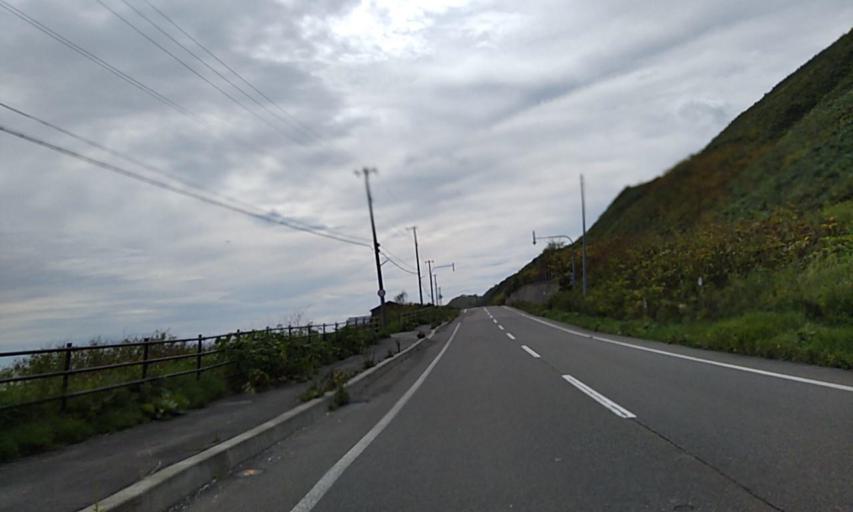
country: JP
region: Hokkaido
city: Kushiro
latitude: 42.8015
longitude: 143.8131
